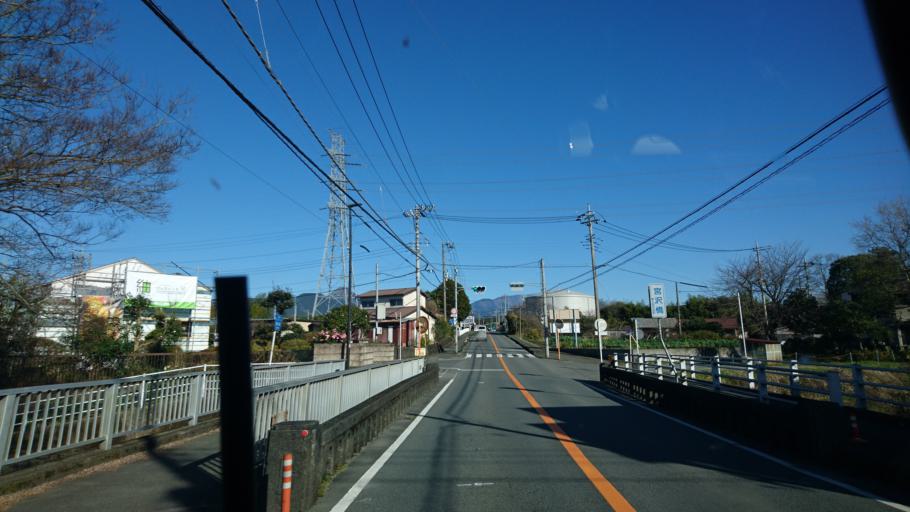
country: JP
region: Shizuoka
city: Fujinomiya
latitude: 35.2541
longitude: 138.6084
